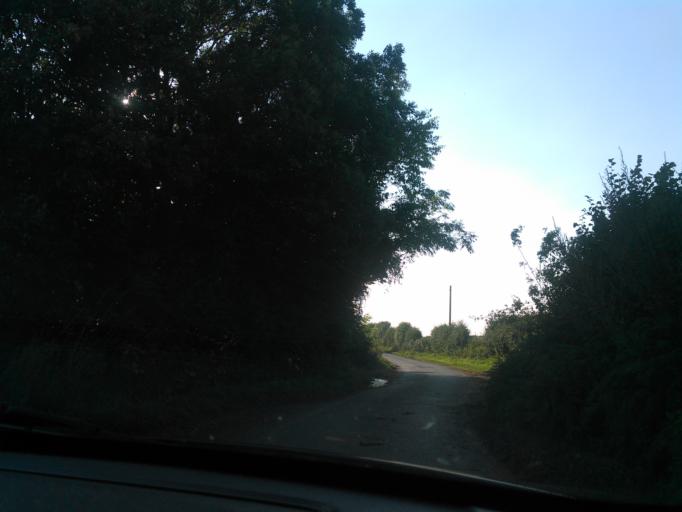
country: GB
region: England
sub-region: Shropshire
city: Stoke upon Tern
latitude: 52.8175
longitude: -2.5900
